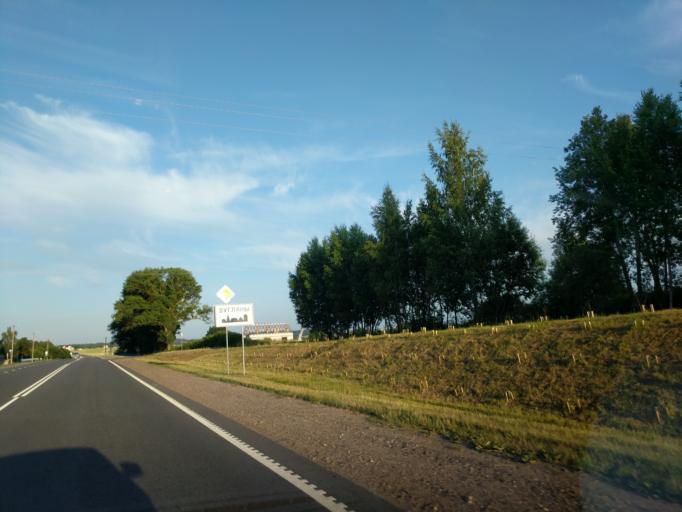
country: BY
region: Minsk
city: Syomkava
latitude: 54.1029
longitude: 27.4763
